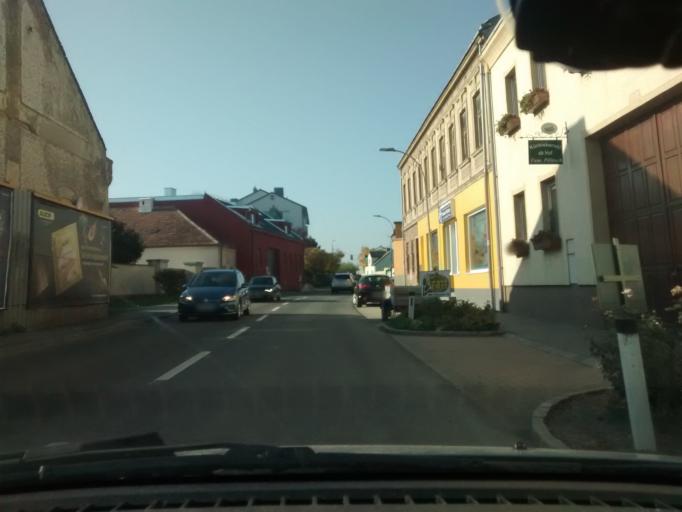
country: AT
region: Lower Austria
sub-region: Politischer Bezirk Modling
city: Achau
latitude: 48.0798
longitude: 16.3829
